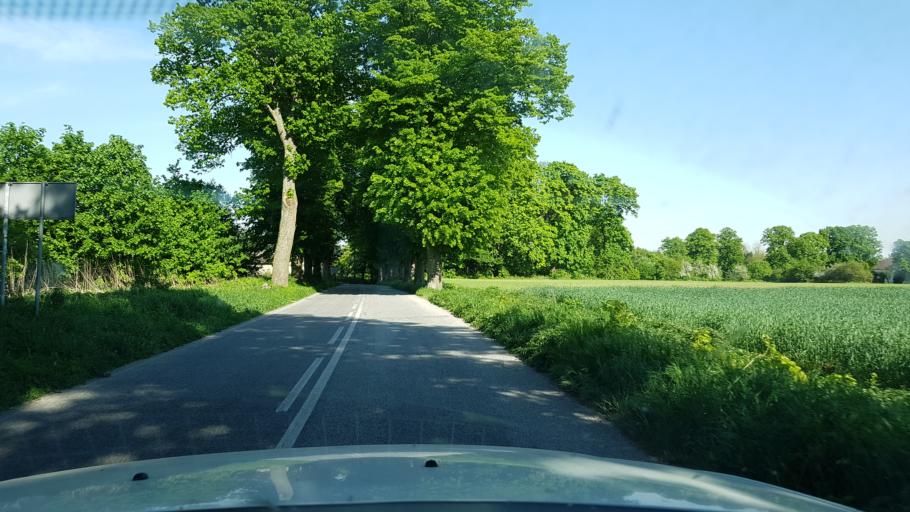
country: PL
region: West Pomeranian Voivodeship
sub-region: Powiat lobeski
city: Resko
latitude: 53.8108
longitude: 15.4156
